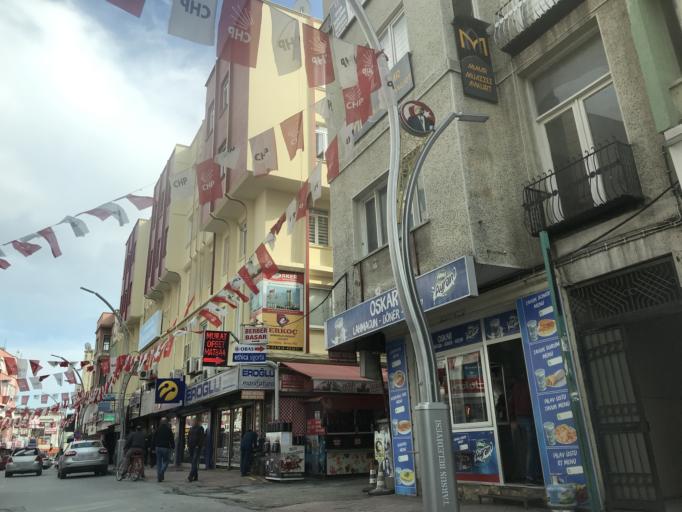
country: TR
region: Mersin
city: Tarsus
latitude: 36.9162
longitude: 34.8926
